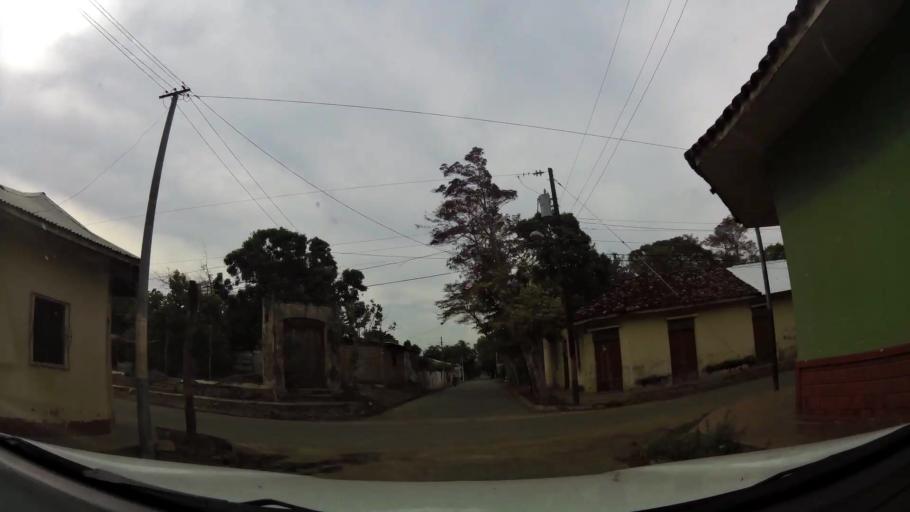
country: NI
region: Rivas
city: San Jorge
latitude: 11.4559
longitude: -85.7992
